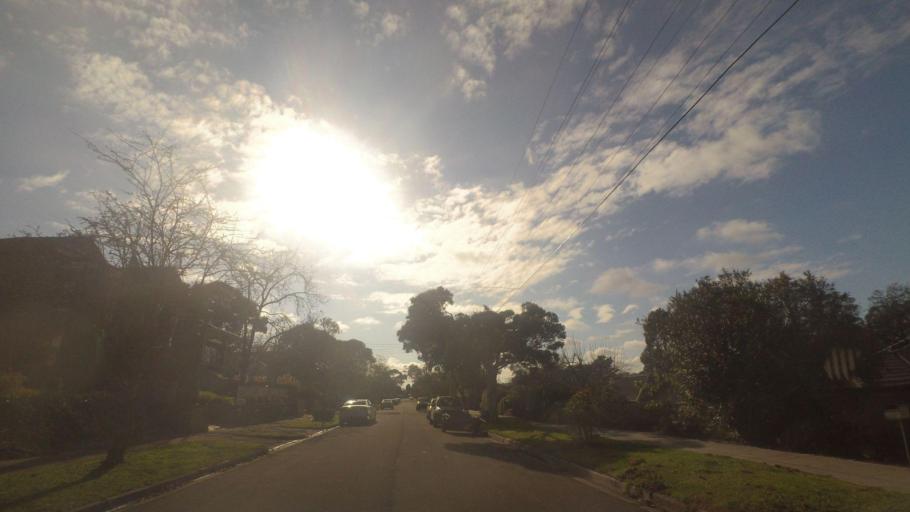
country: AU
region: Victoria
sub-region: Whitehorse
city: Mont Albert North
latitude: -37.7982
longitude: 145.1080
